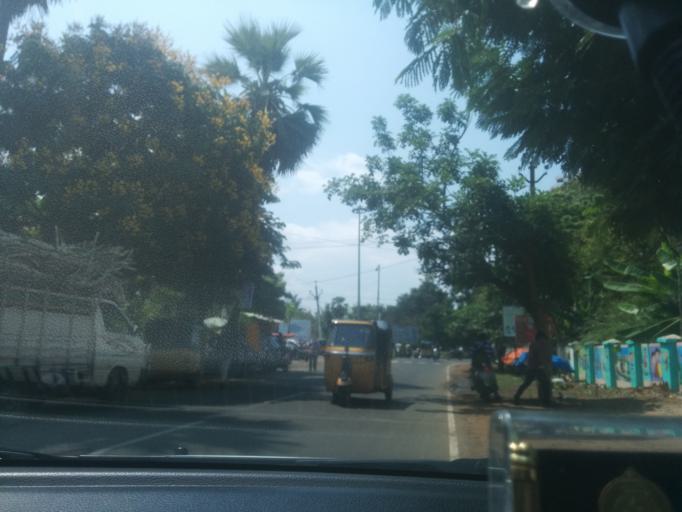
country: IN
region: Andhra Pradesh
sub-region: East Godavari
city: Rajahmundry
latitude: 17.0206
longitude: 81.7938
